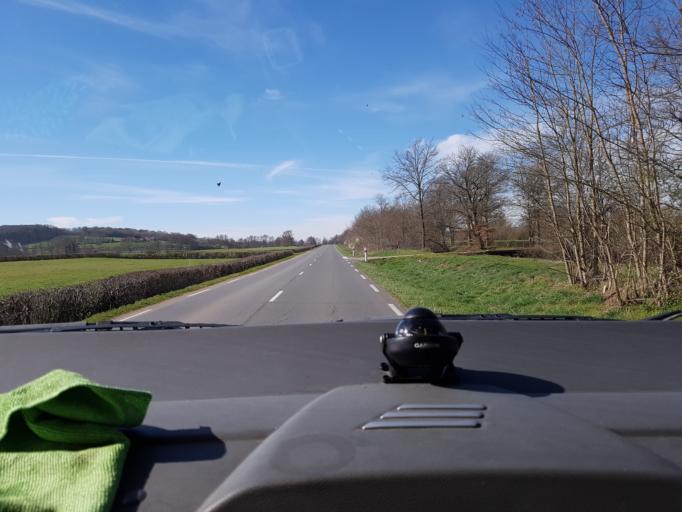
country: FR
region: Bourgogne
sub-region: Departement de Saone-et-Loire
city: Gueugnon
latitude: 46.5628
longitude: 4.0516
